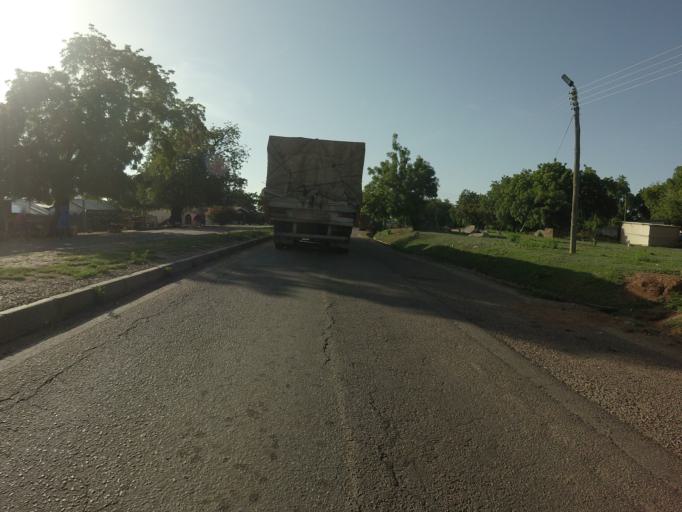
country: GH
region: Upper East
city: Navrongo
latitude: 10.8984
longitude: -1.0923
